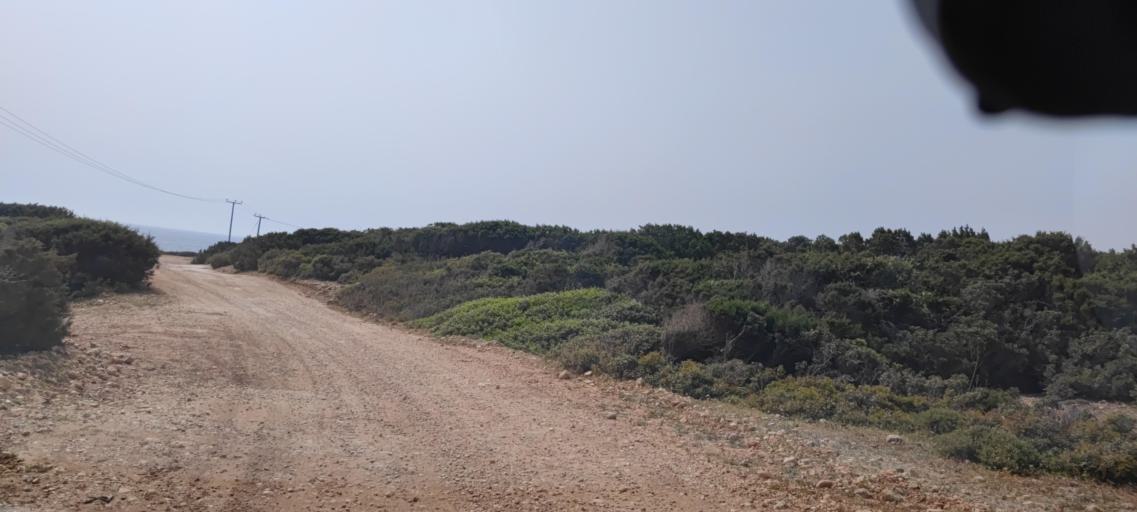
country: CY
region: Ammochostos
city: Rizokarpaso
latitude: 35.6792
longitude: 34.5765
